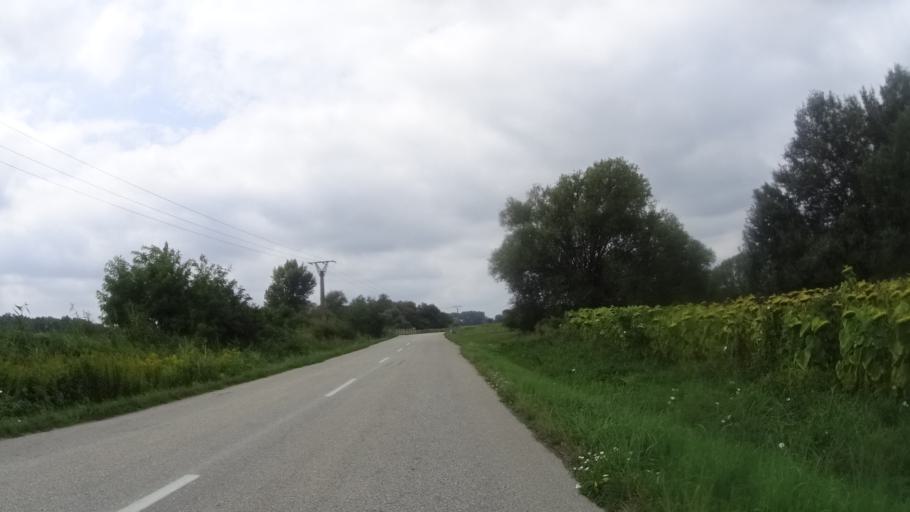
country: HU
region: Gyor-Moson-Sopron
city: Bony
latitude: 47.7513
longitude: 17.8627
